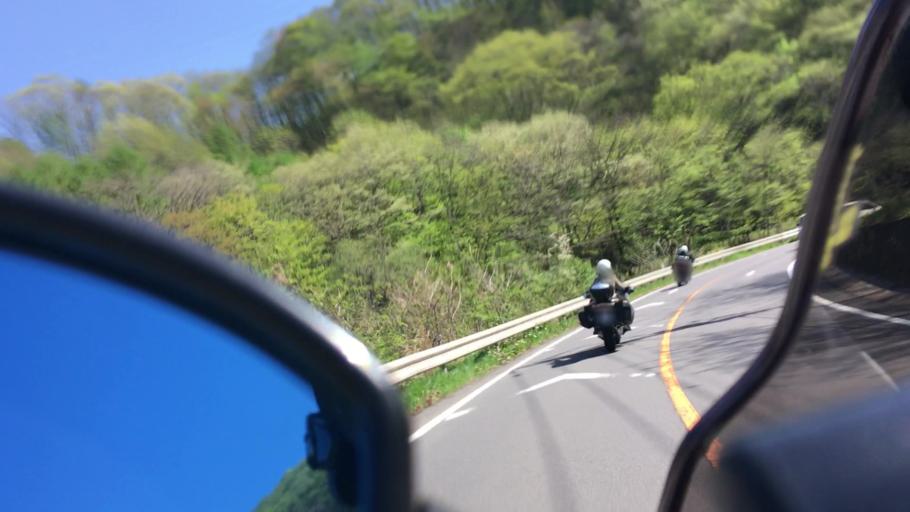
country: JP
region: Nagano
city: Komoro
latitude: 36.4875
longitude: 138.4864
